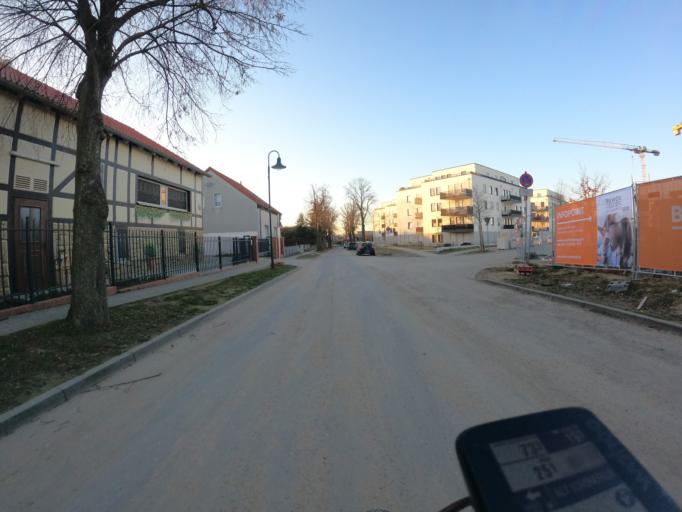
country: DE
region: Brandenburg
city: Schonefeld
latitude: 52.3917
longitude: 13.5024
